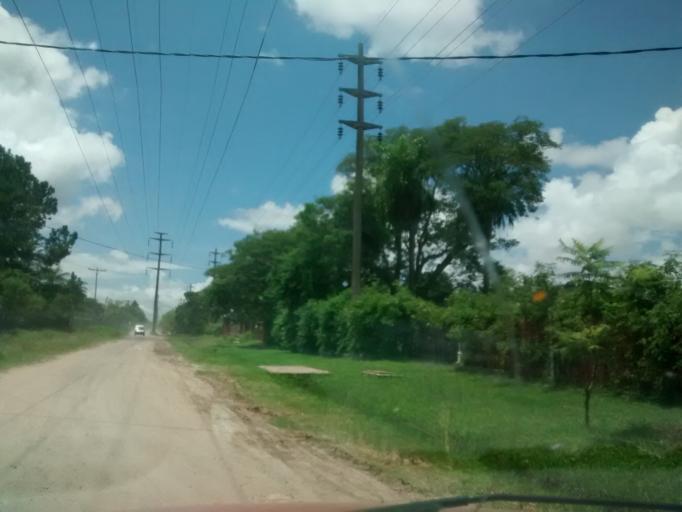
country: AR
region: Chaco
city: Fontana
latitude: -27.4162
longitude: -58.9828
